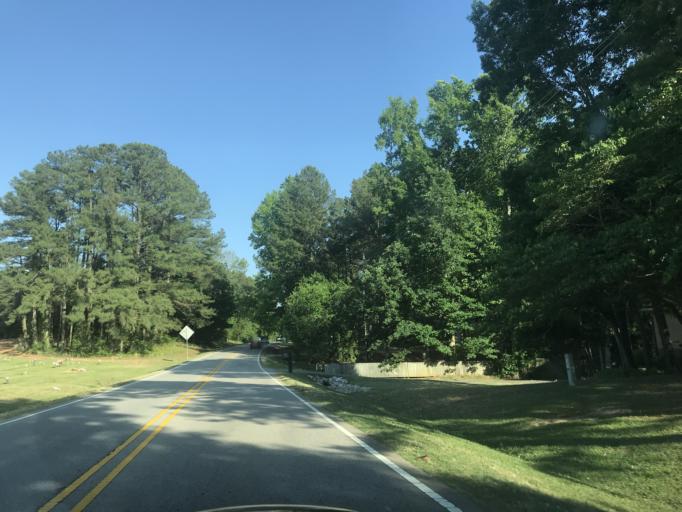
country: US
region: North Carolina
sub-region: Wake County
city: Garner
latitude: 35.7344
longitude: -78.6045
